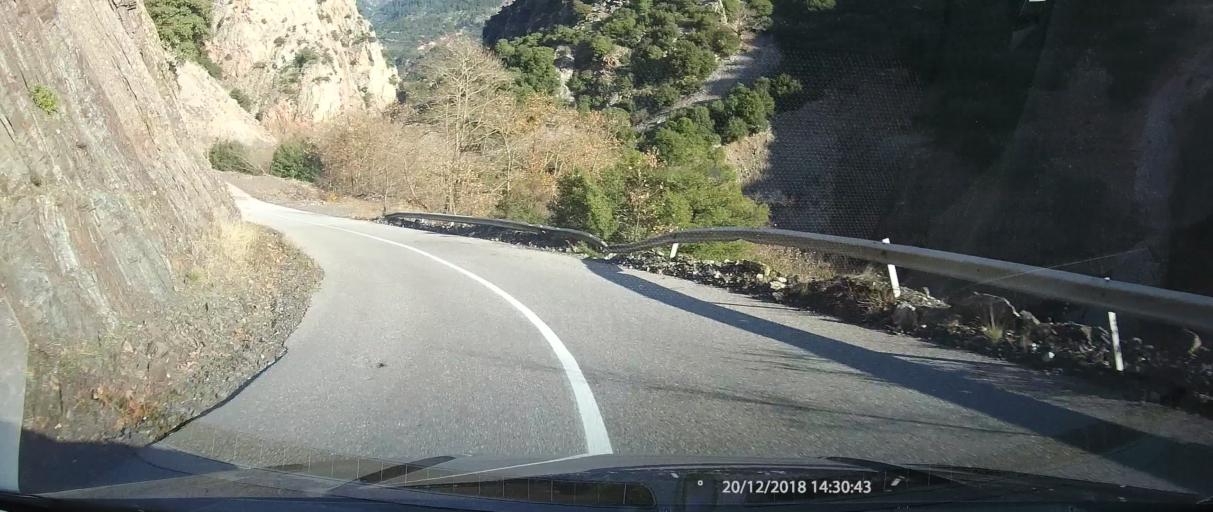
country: GR
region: Central Greece
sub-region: Nomos Evrytanias
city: Karpenisi
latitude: 38.7900
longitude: 21.6971
